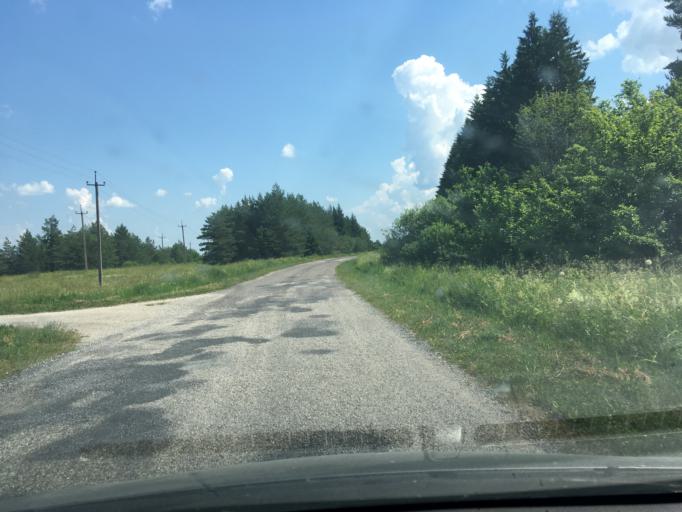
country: EE
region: Laeaene
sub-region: Lihula vald
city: Lihula
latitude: 58.6665
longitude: 23.7526
